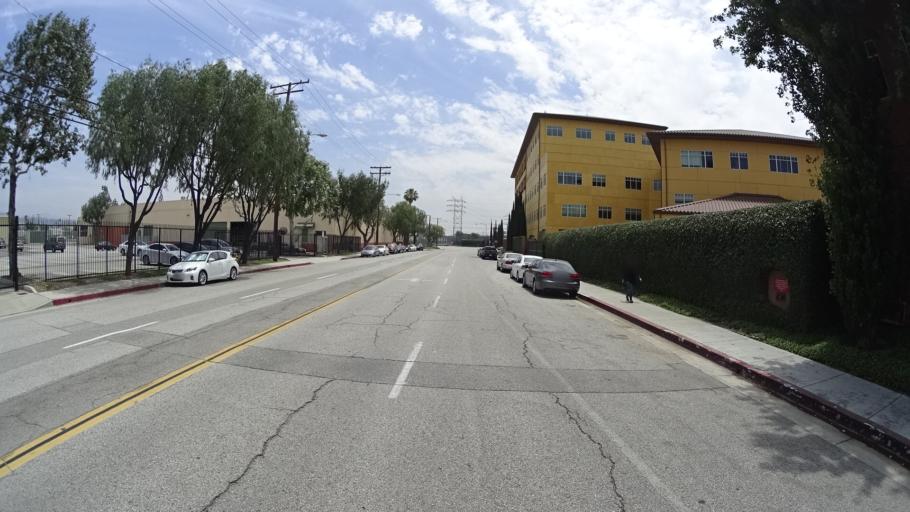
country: US
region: California
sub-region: Los Angeles County
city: North Glendale
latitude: 34.1579
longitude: -118.2847
